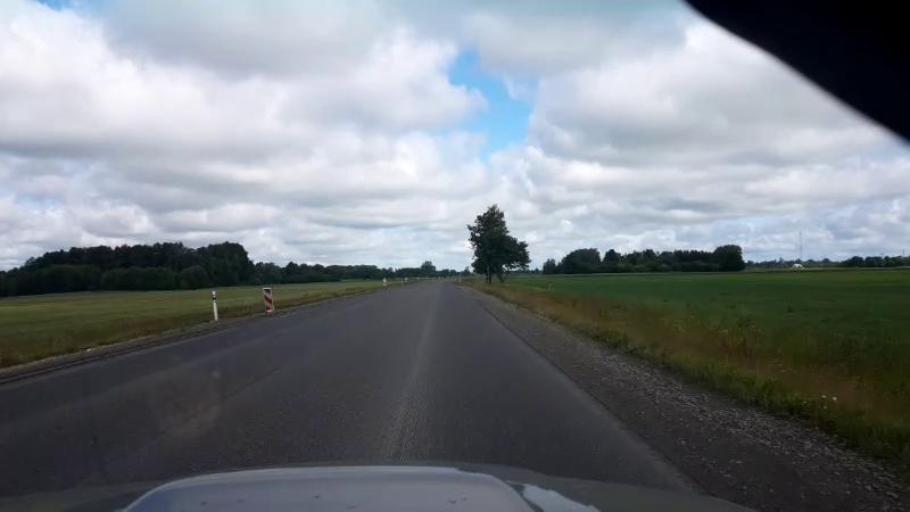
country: LV
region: Bauskas Rajons
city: Bauska
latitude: 56.2950
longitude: 24.3476
